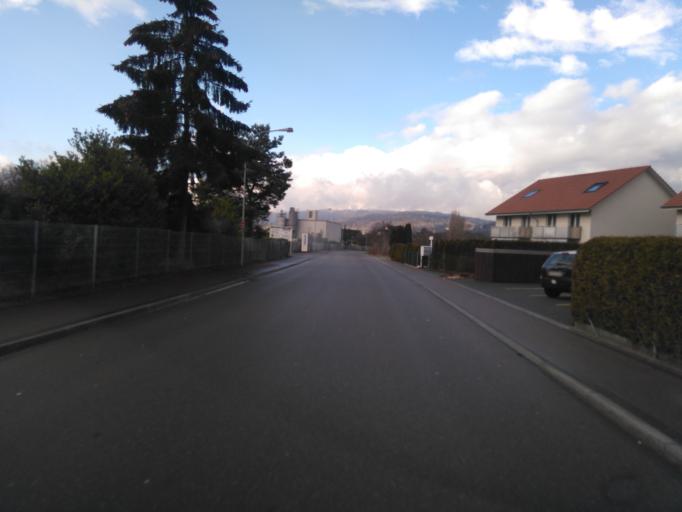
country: CH
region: Zurich
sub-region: Bezirk Dielsdorf
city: Regensdorf / Feldblumen-Riedthofstrasse
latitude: 47.4424
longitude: 8.4722
